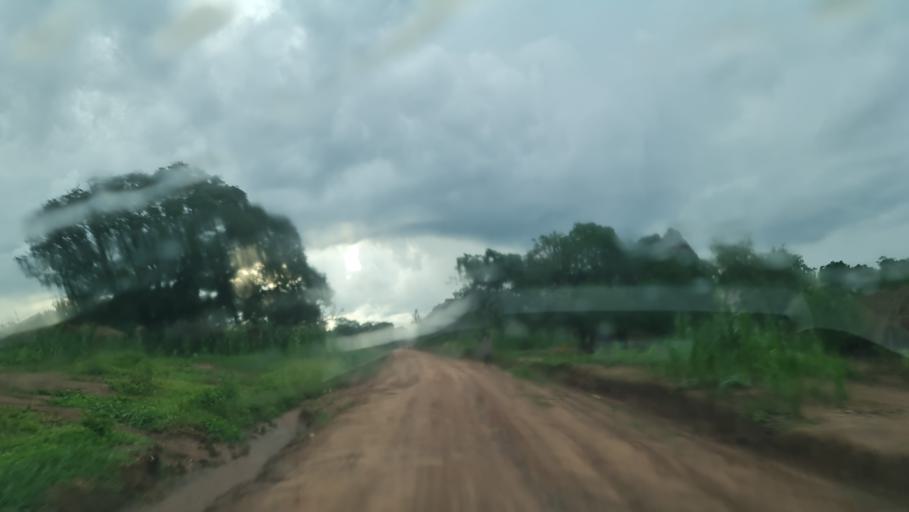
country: MZ
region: Nampula
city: Nacala
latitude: -13.9843
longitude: 40.3942
